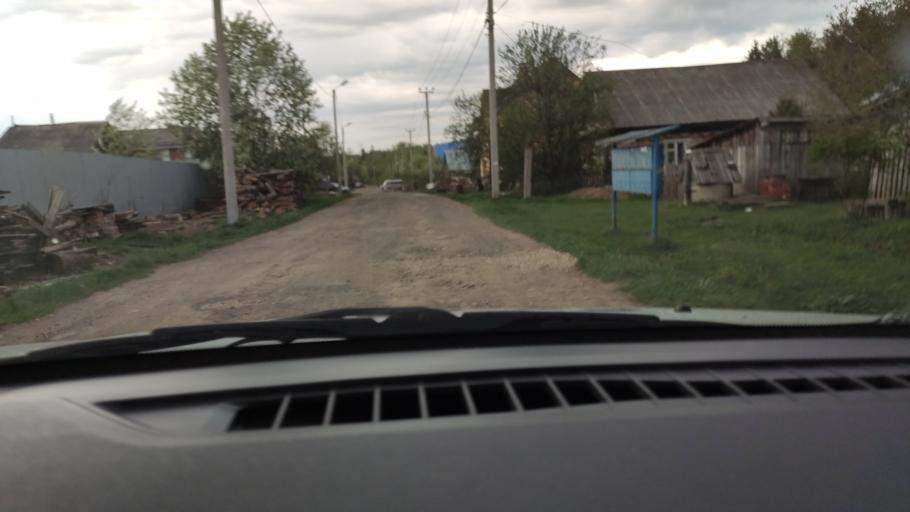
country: RU
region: Perm
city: Froly
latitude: 57.9538
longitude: 56.2901
